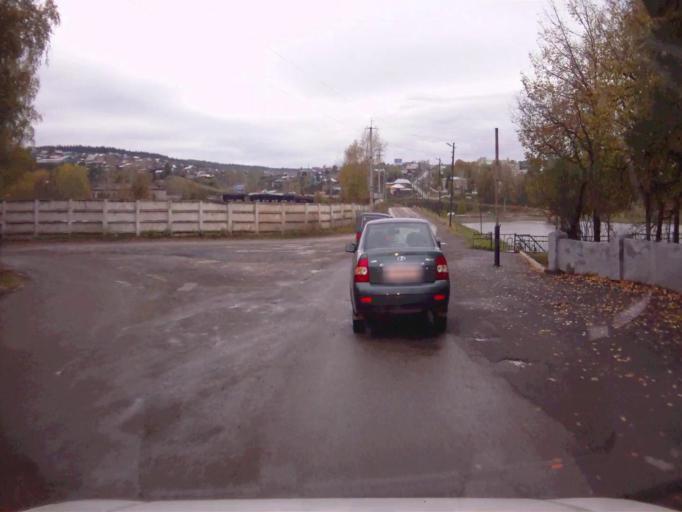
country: RU
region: Chelyabinsk
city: Nyazepetrovsk
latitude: 56.0542
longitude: 59.5942
